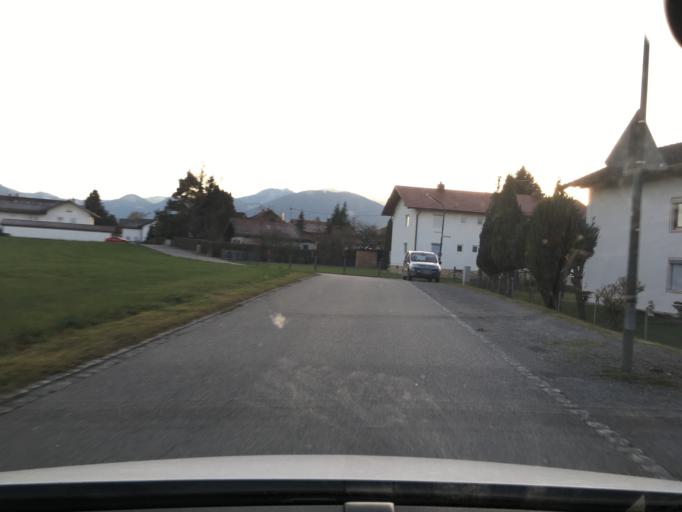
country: DE
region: Bavaria
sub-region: Upper Bavaria
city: Raubling
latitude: 47.7906
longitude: 12.1034
